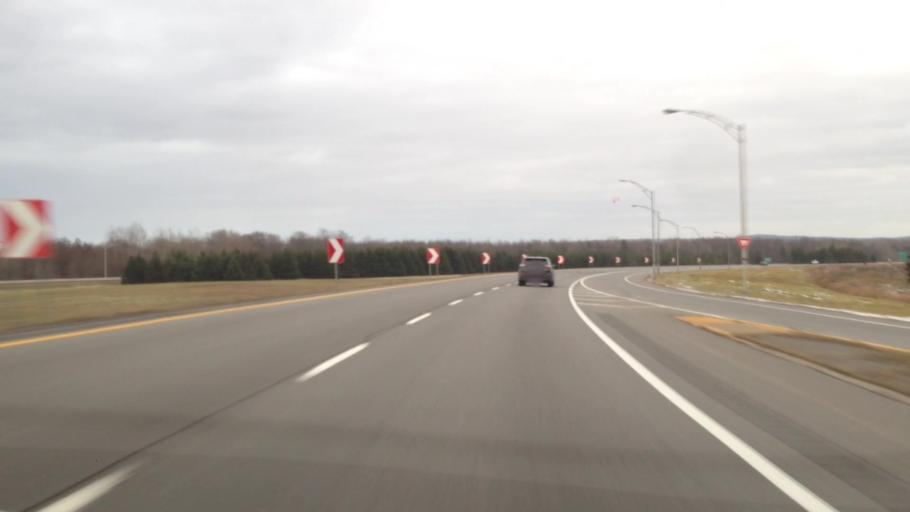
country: CA
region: Quebec
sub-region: Monteregie
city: Rigaud
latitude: 45.5366
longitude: -74.3838
